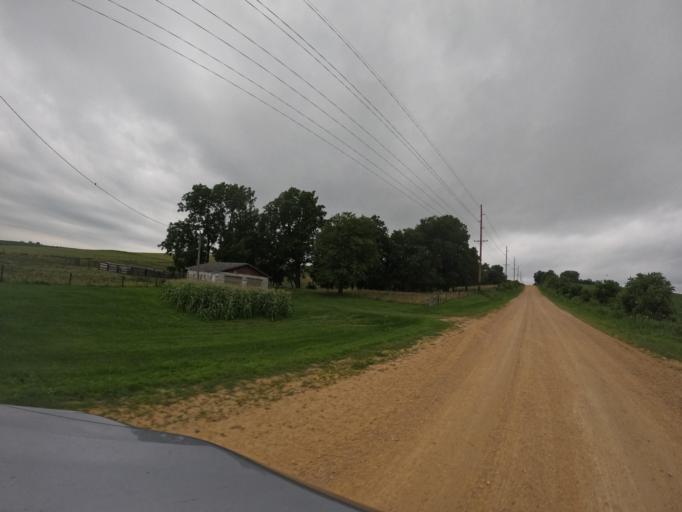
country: US
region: Iowa
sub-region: Jackson County
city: Maquoketa
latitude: 41.9381
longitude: -90.6276
